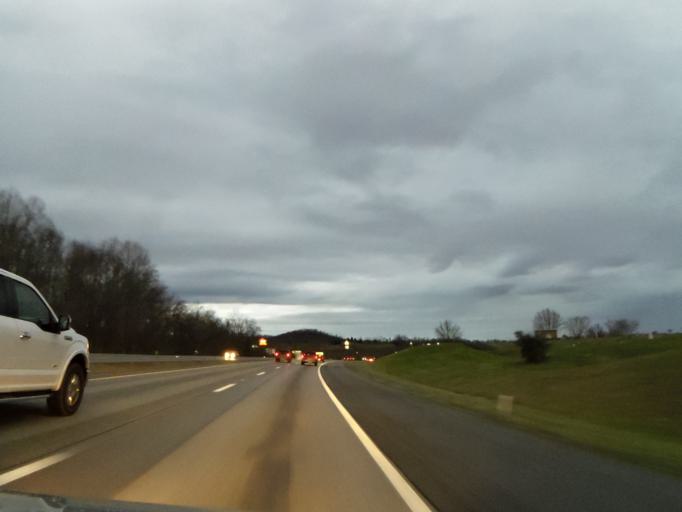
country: US
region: Tennessee
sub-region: Washington County
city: Oak Grove
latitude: 36.3724
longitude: -82.4222
